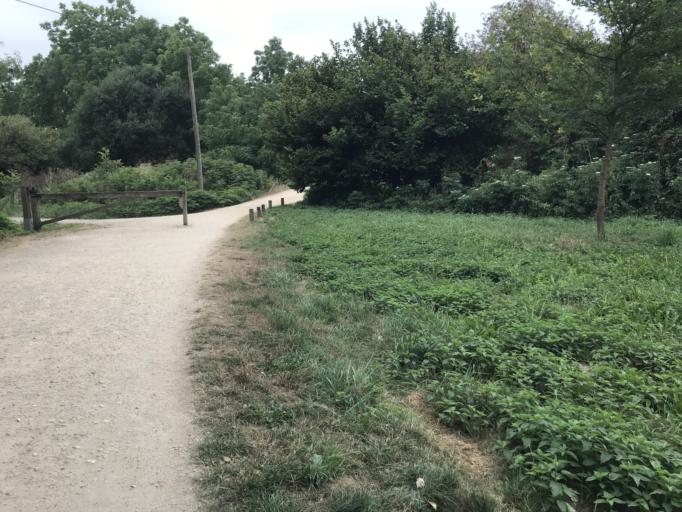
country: ES
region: Basque Country
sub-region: Provincia de Alava
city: Gasteiz / Vitoria
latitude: 42.8528
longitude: -2.6367
